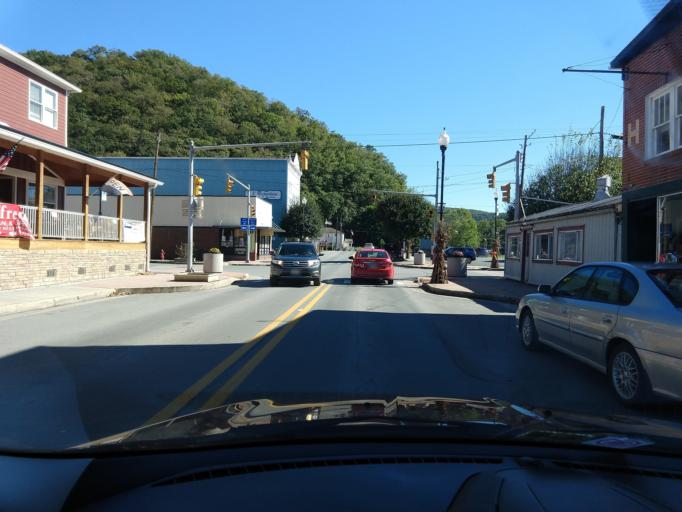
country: US
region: West Virginia
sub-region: Pocahontas County
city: Marlinton
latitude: 38.2232
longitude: -80.0939
